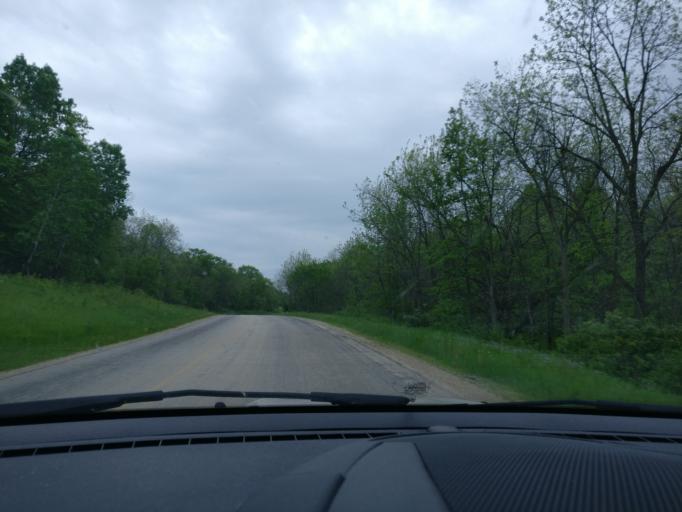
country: US
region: Wisconsin
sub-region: Lafayette County
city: Darlington
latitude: 42.7602
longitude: -90.0094
